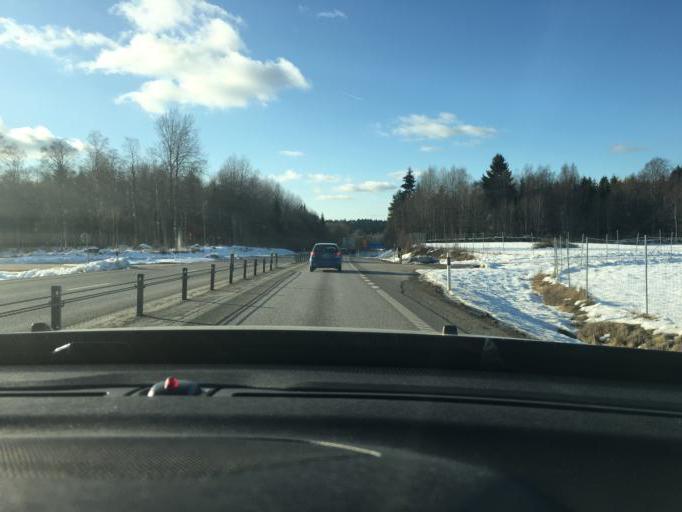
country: SE
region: Vaestra Goetaland
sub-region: Ulricehamns Kommun
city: Ulricehamn
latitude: 57.7956
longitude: 13.5480
